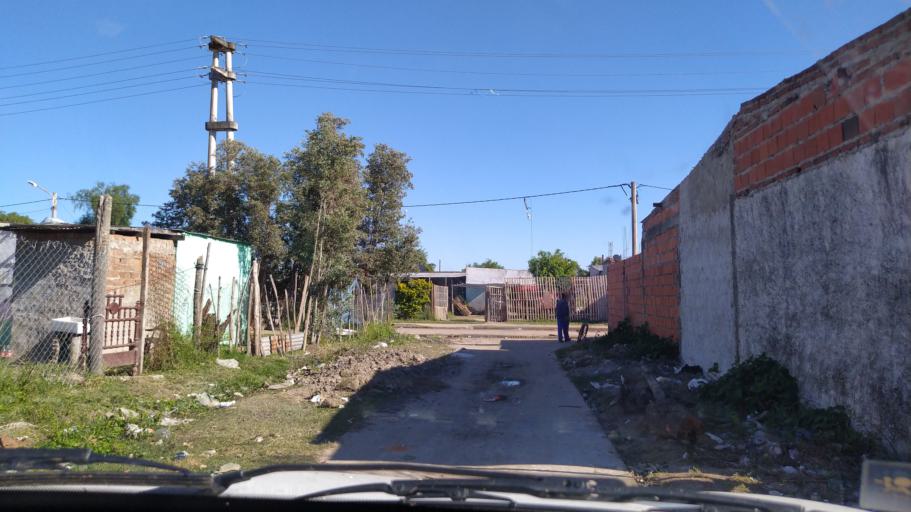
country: AR
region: Corrientes
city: Corrientes
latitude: -27.4989
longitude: -58.8078
